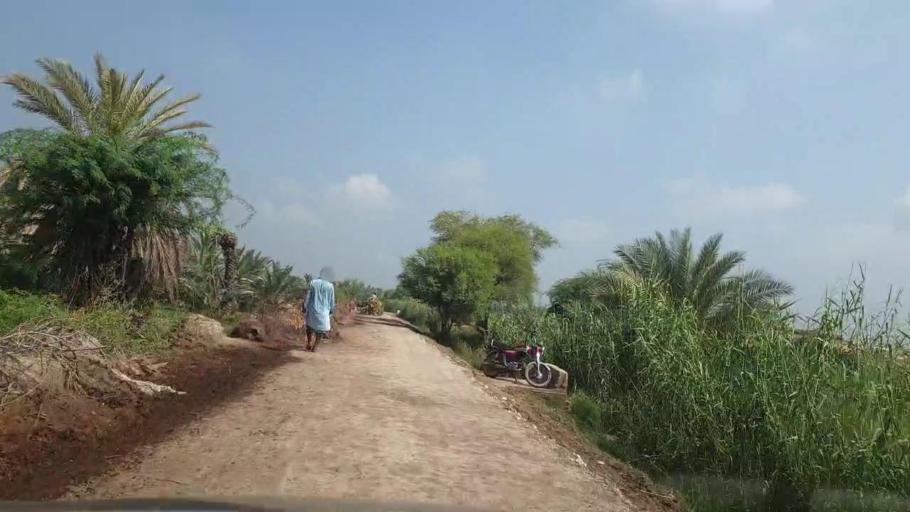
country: PK
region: Sindh
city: Pir jo Goth
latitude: 27.5984
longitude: 68.6935
